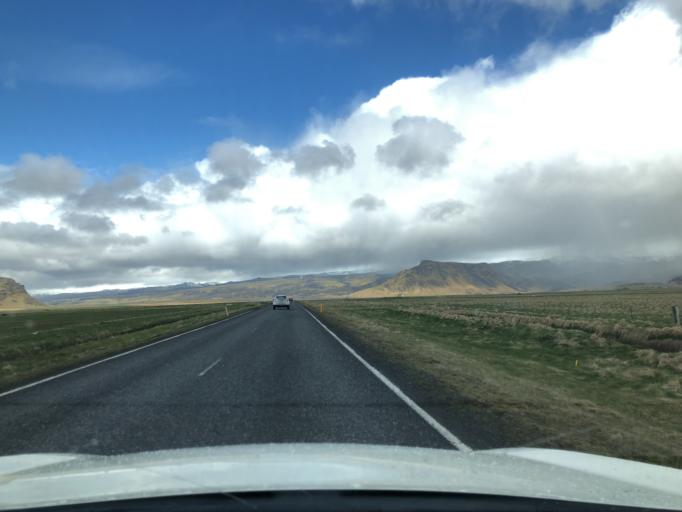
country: IS
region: South
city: Vestmannaeyjar
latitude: 63.4461
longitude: -19.2028
